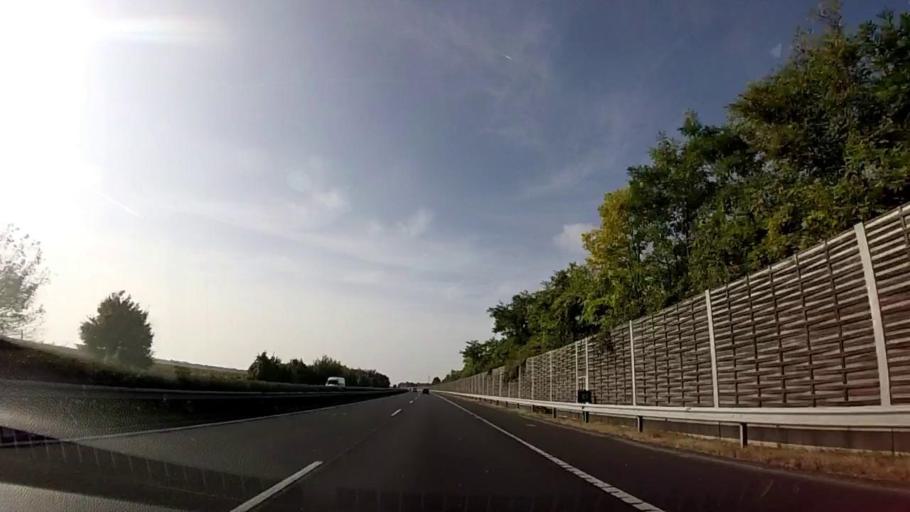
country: HU
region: Fejer
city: Lepseny
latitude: 46.9841
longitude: 18.1786
